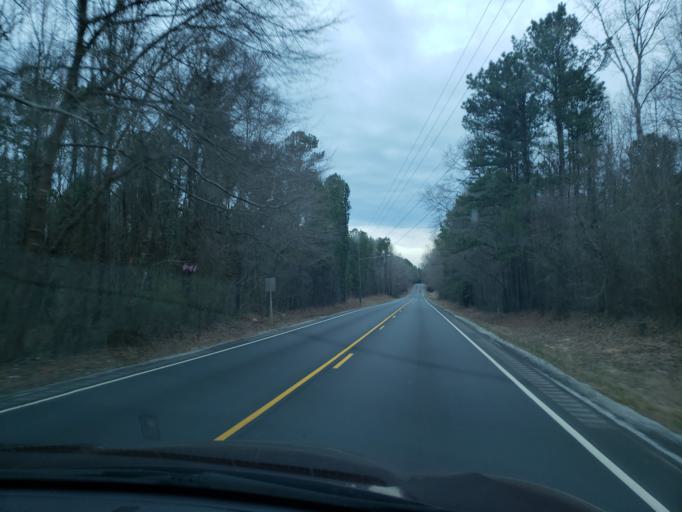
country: US
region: Alabama
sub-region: Randolph County
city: Roanoke
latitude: 33.0221
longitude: -85.3495
